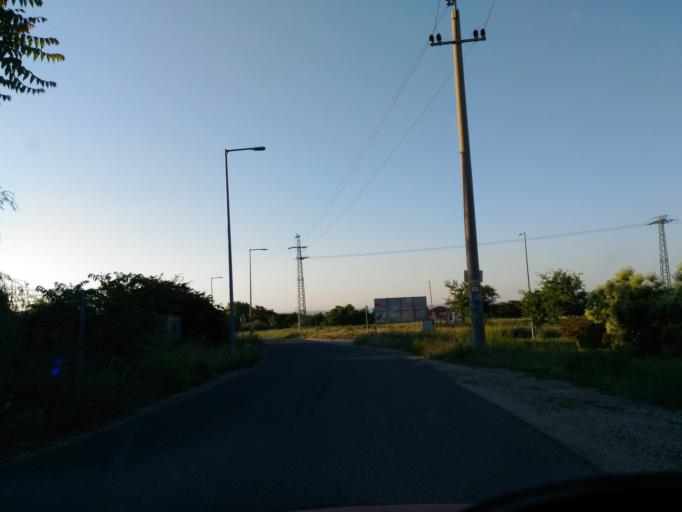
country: HU
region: Pest
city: Diosd
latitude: 47.4170
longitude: 18.9435
